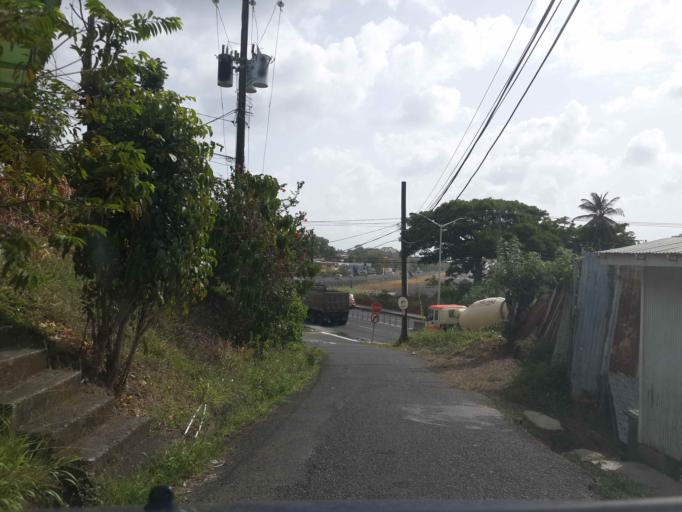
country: LC
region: Castries Quarter
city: Bisee
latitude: 14.0226
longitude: -60.9831
